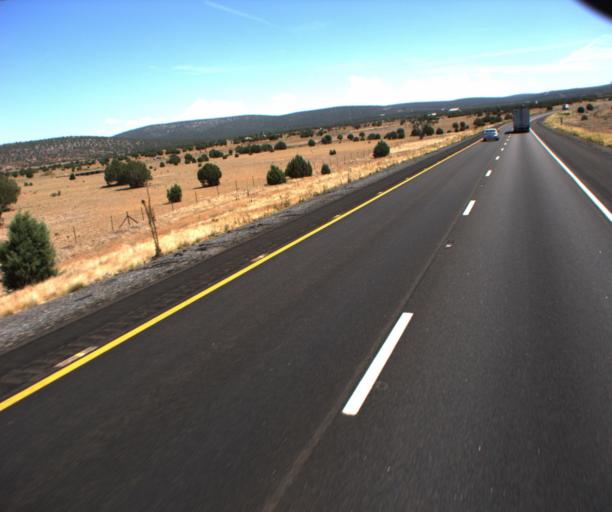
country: US
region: Arizona
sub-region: Mohave County
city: Peach Springs
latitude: 35.1872
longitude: -113.3782
